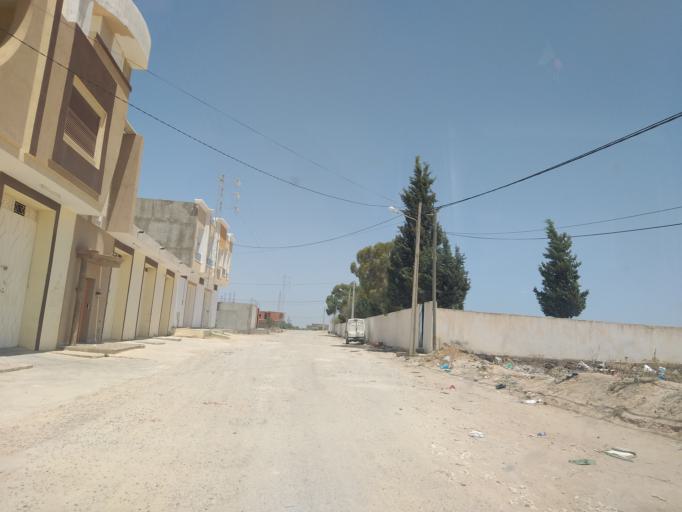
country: TN
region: Al Mahdiyah
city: El Jem
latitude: 35.3097
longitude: 10.7038
